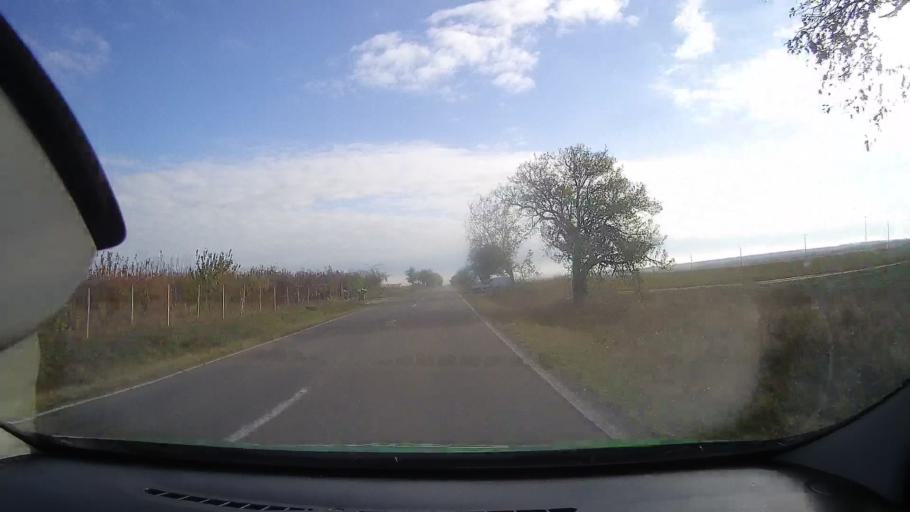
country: RO
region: Tulcea
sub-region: Comuna Mahmudia
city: Mahmudia
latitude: 45.0776
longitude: 29.0650
